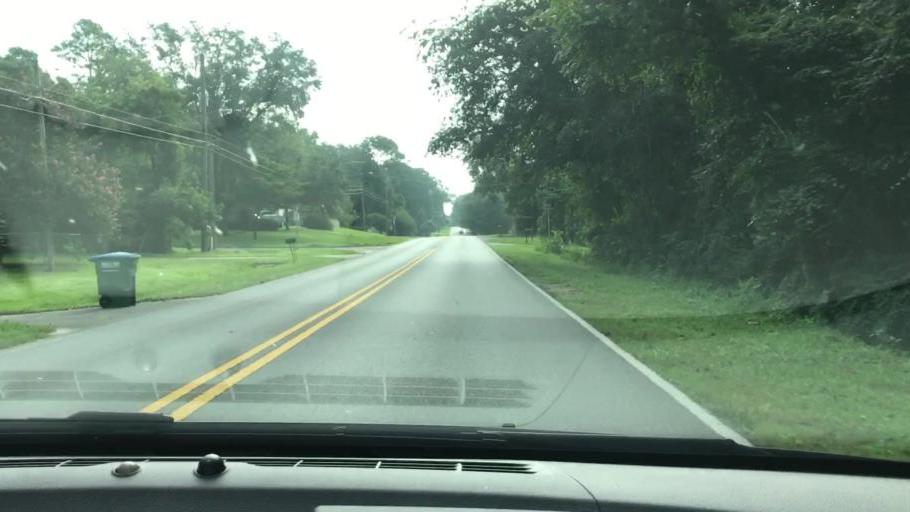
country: US
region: Florida
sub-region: Jackson County
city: Marianna
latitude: 30.7689
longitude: -85.2383
